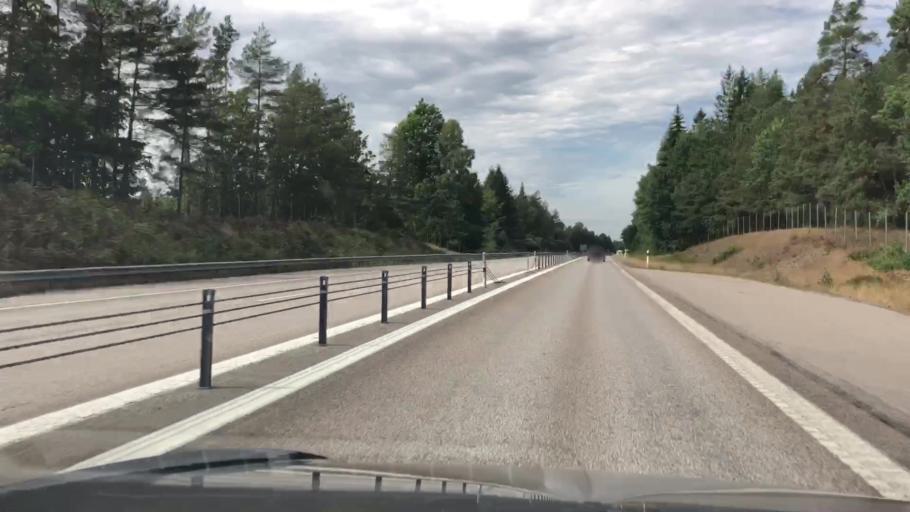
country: SE
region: Blekinge
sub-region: Ronneby Kommun
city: Brakne-Hoby
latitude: 56.2179
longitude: 15.1769
